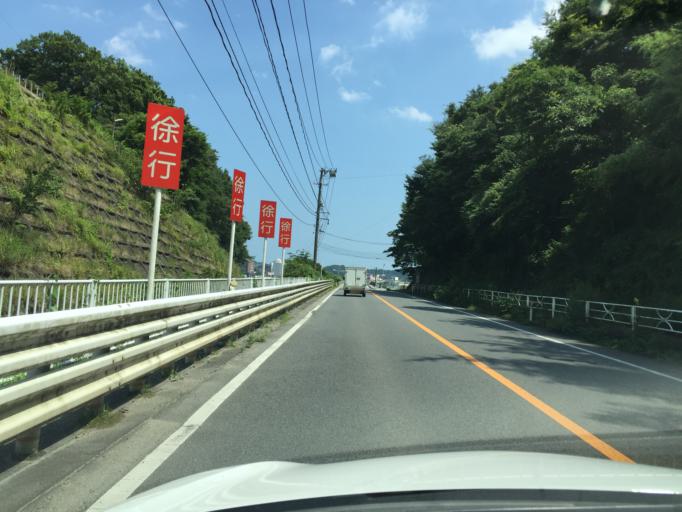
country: JP
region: Fukushima
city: Iwaki
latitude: 37.0559
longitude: 140.8745
